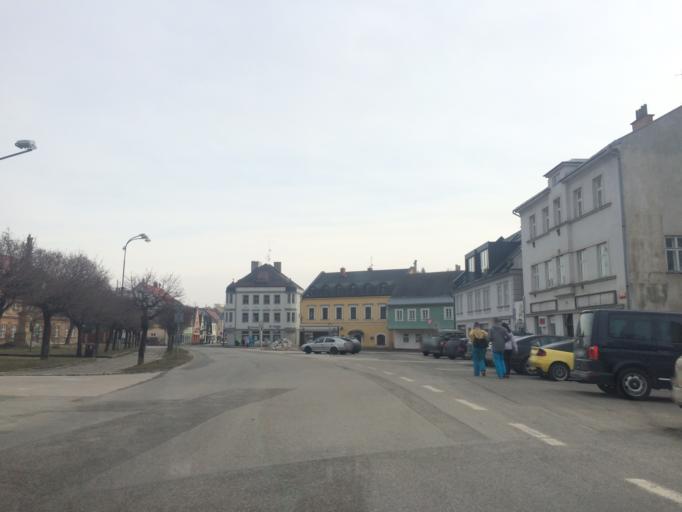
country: CZ
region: Kralovehradecky
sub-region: Okres Trutnov
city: Vrchlabi
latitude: 50.6297
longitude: 15.6073
